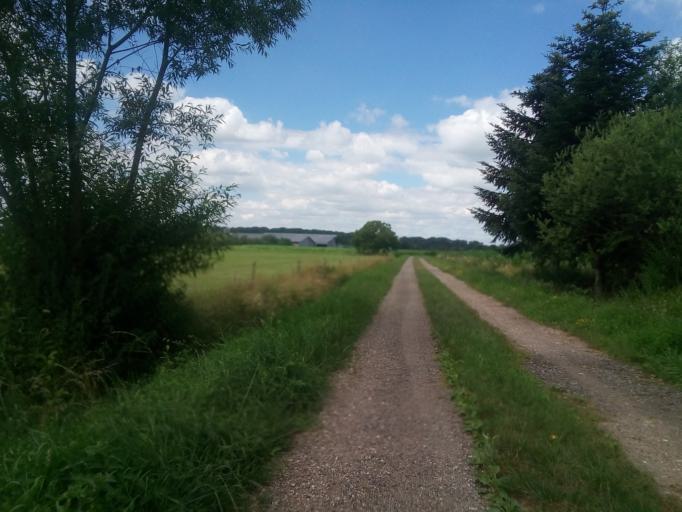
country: DE
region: Baden-Wuerttemberg
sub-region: Freiburg Region
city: Renchen
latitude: 48.6204
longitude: 7.9804
